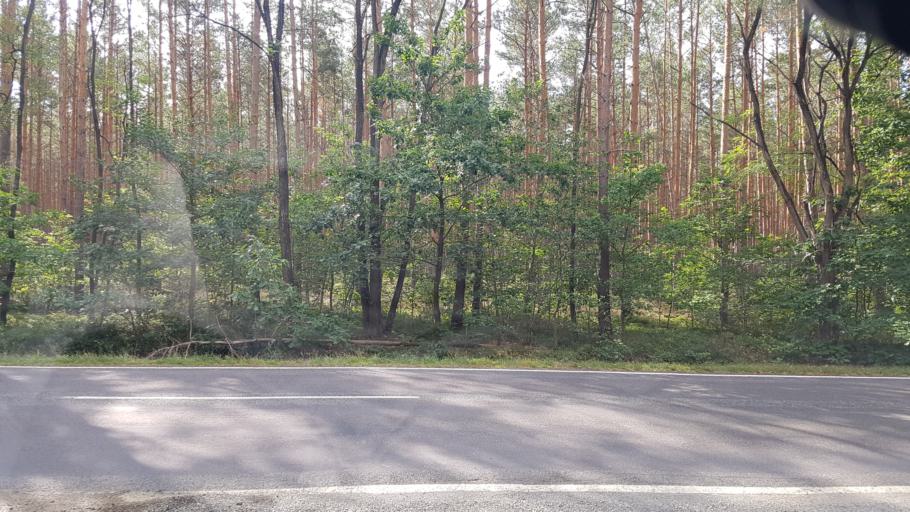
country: DE
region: Brandenburg
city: Ruckersdorf
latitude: 51.5599
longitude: 13.6335
